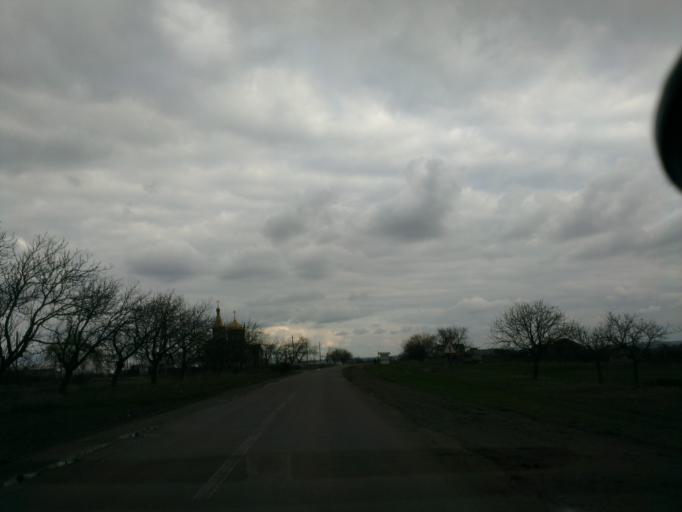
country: MD
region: Gagauzia
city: Comrat
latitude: 46.3068
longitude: 28.6194
